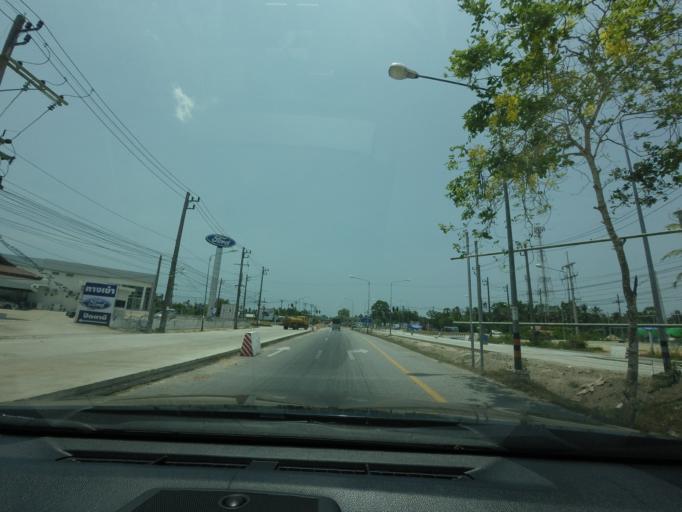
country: TH
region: Pattani
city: Pattani
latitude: 6.8534
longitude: 101.2229
